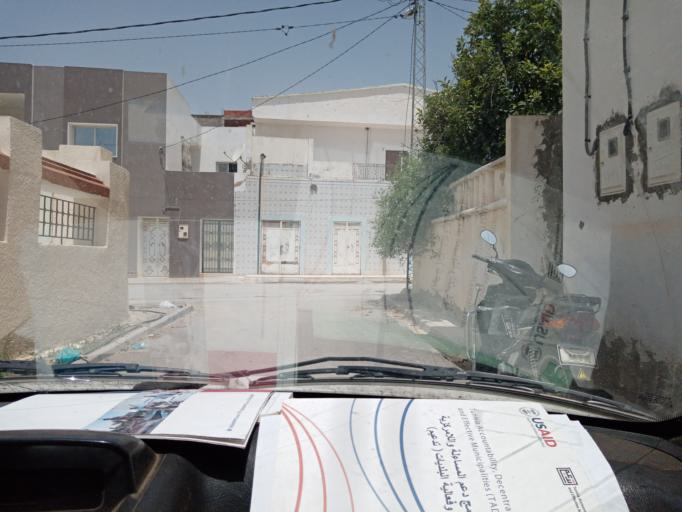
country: TN
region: Al Qayrawan
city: Sbikha
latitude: 36.1158
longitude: 10.0959
